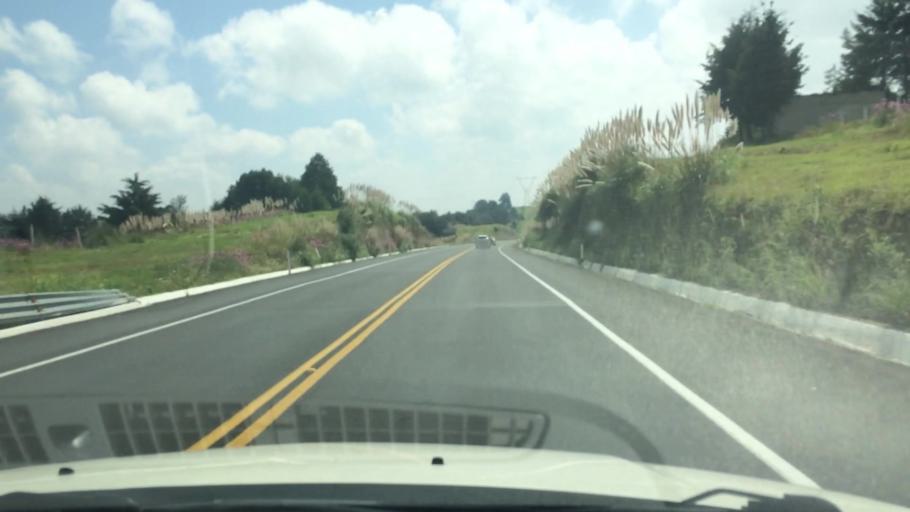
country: MX
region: Mexico
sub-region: Almoloya de Juarez
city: San Pedro de la Hortaliza (Ejido Almoloyan)
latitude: 19.3788
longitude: -99.8564
